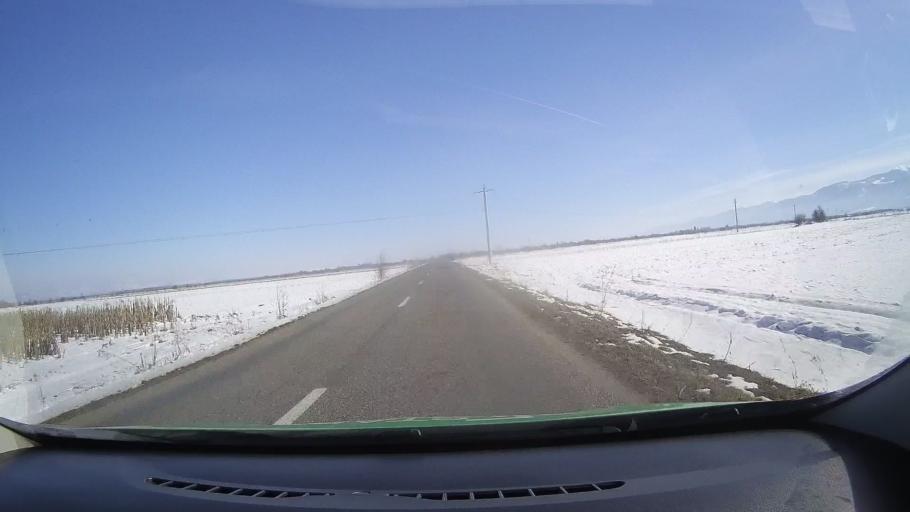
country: RO
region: Brasov
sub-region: Comuna Lisa
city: Lisa
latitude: 45.7271
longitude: 24.8811
